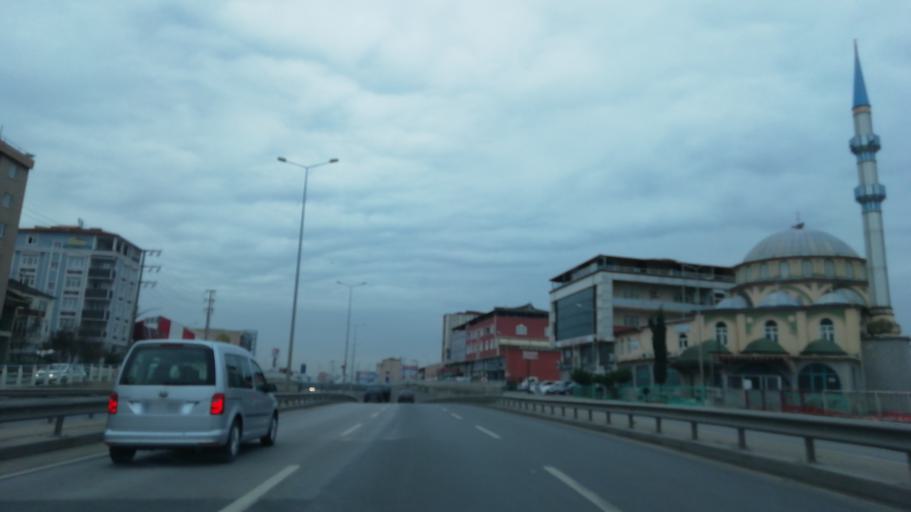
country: TR
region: Kocaeli
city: Korfez
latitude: 40.7586
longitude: 29.7938
